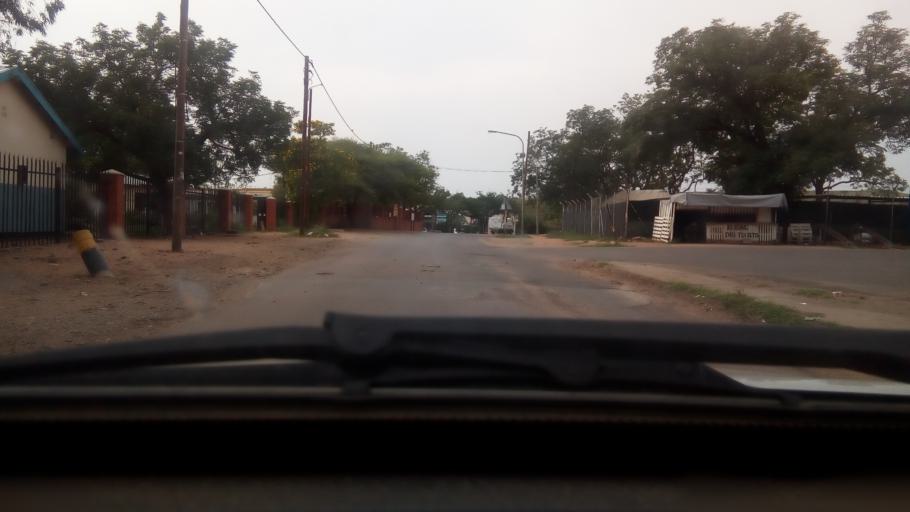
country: BW
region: South East
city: Gaborone
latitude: -24.6673
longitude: 25.9412
